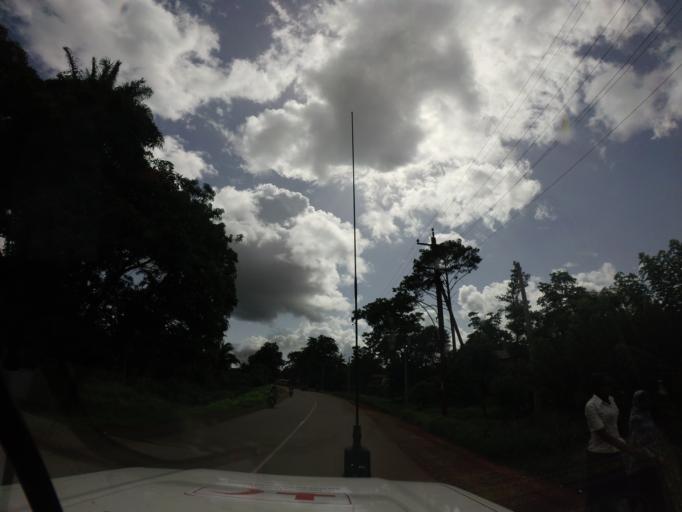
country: GN
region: Mamou
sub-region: Mamou Prefecture
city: Mamou
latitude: 10.3715
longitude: -12.0721
